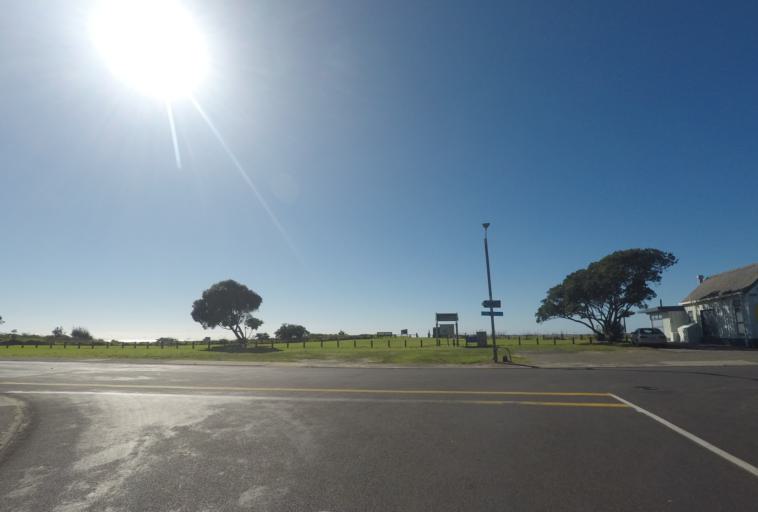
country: NZ
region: Waikato
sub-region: Thames-Coromandel District
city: Whangamata
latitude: -37.2824
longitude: 175.9020
